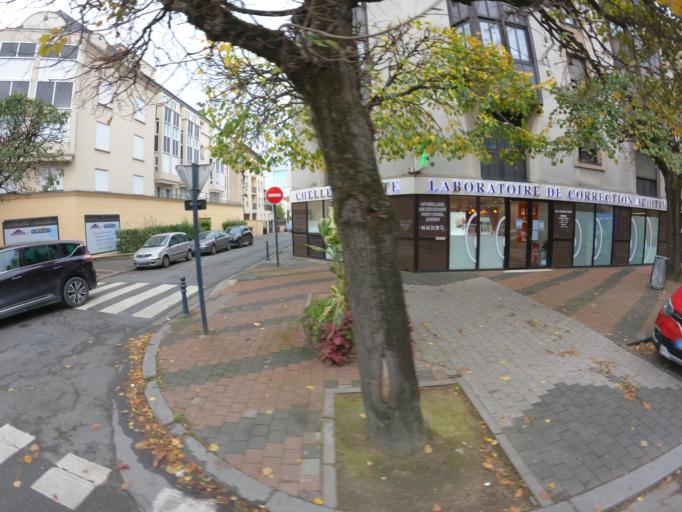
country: FR
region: Ile-de-France
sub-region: Departement de Seine-Saint-Denis
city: Gournay-sur-Marne
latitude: 48.8717
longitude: 2.5778
